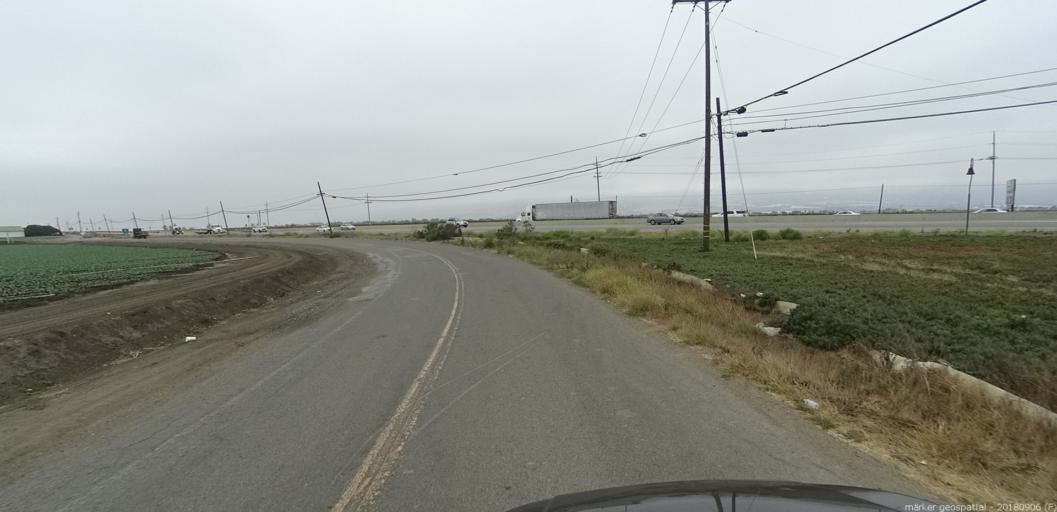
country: US
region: California
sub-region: Monterey County
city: Chualar
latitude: 36.6247
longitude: -121.5821
